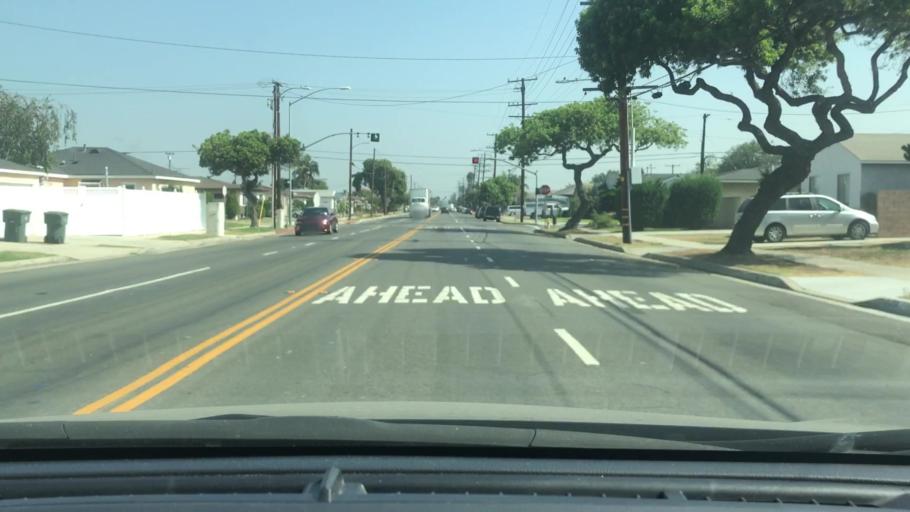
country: US
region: California
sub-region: Los Angeles County
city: Gardena
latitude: 33.8813
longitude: -118.3178
